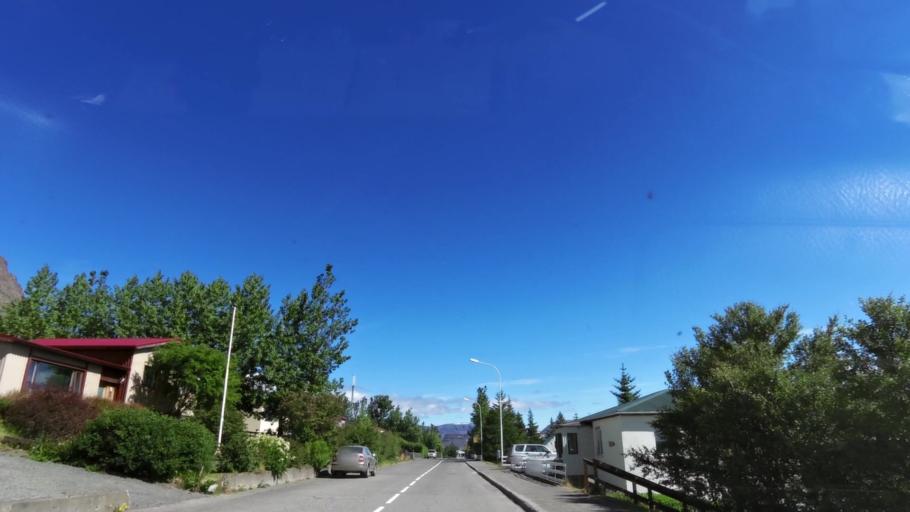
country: IS
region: Westfjords
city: Isafjoerdur
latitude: 65.6838
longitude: -23.6055
